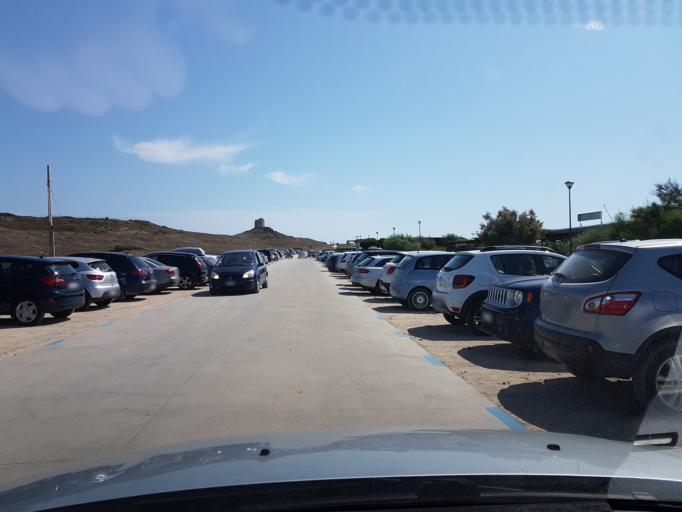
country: IT
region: Sardinia
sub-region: Provincia di Oristano
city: Cabras
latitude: 39.8802
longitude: 8.4394
